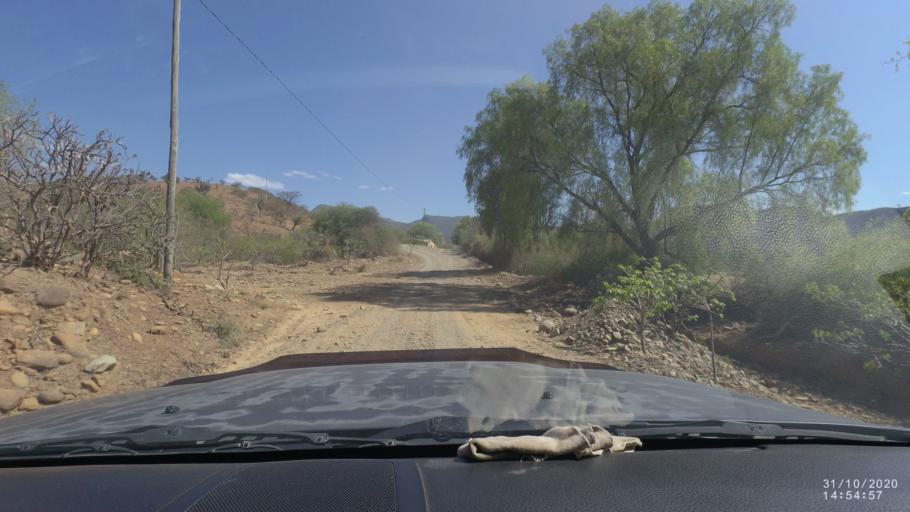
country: BO
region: Cochabamba
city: Aiquile
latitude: -18.2299
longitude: -64.8577
